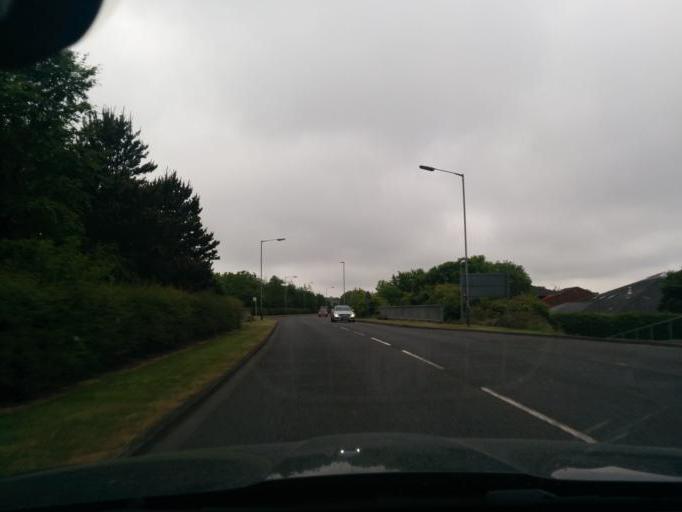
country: GB
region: England
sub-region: Northumberland
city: Cramlington
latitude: 55.0979
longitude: -1.5767
